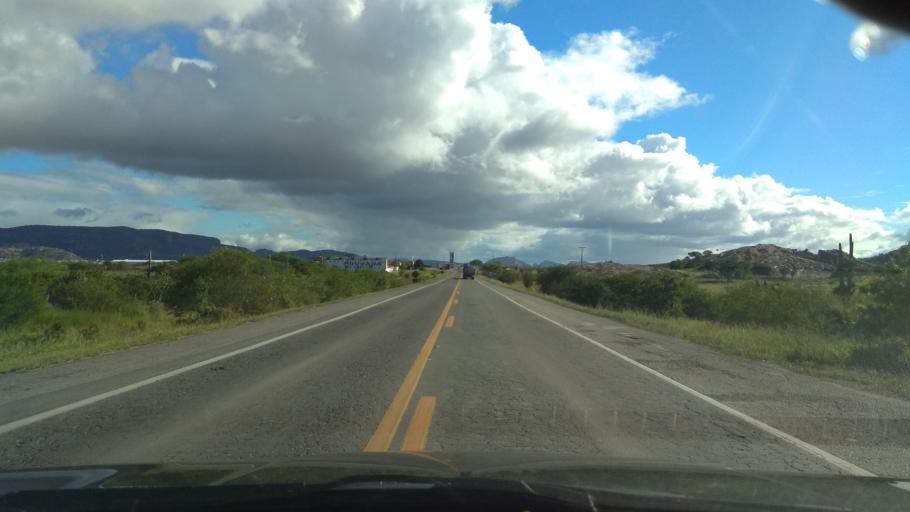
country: BR
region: Bahia
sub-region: Castro Alves
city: Castro Alves
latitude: -12.6853
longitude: -39.6808
